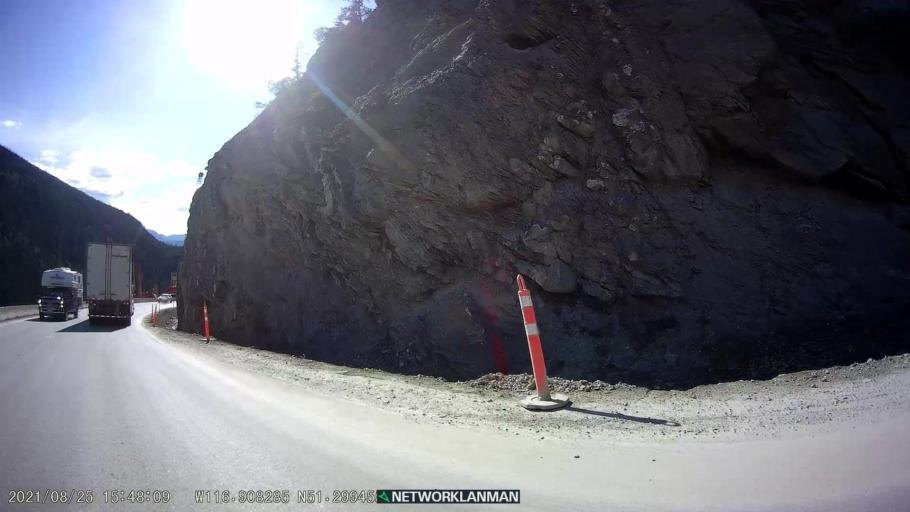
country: CA
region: British Columbia
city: Golden
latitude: 51.2996
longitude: -116.9088
